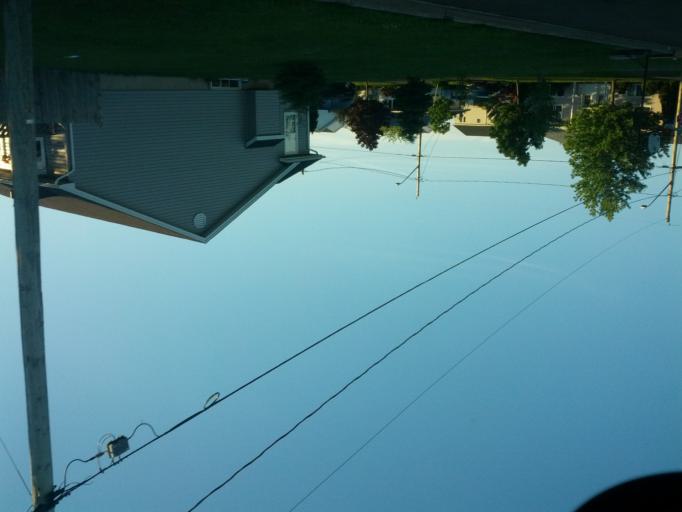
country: CA
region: New Brunswick
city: Moncton
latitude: 46.1195
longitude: -64.8513
